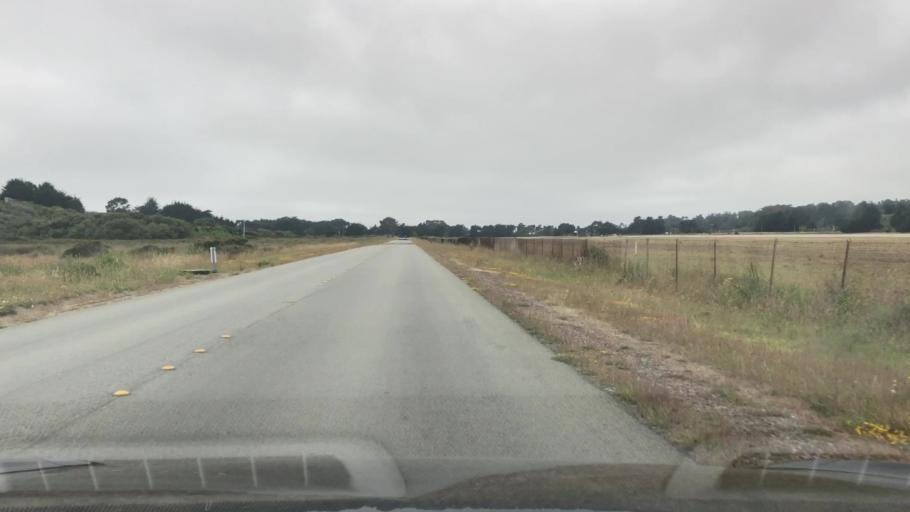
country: US
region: California
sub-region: San Mateo County
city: Moss Beach
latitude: 37.5137
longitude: -122.5054
